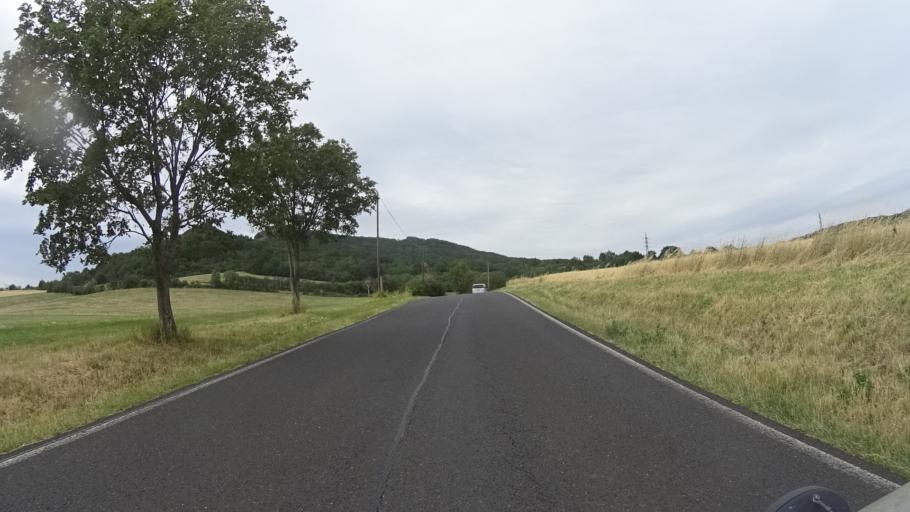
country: CZ
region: Ustecky
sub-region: Okres Litomerice
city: Litomerice
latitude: 50.5600
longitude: 14.1218
